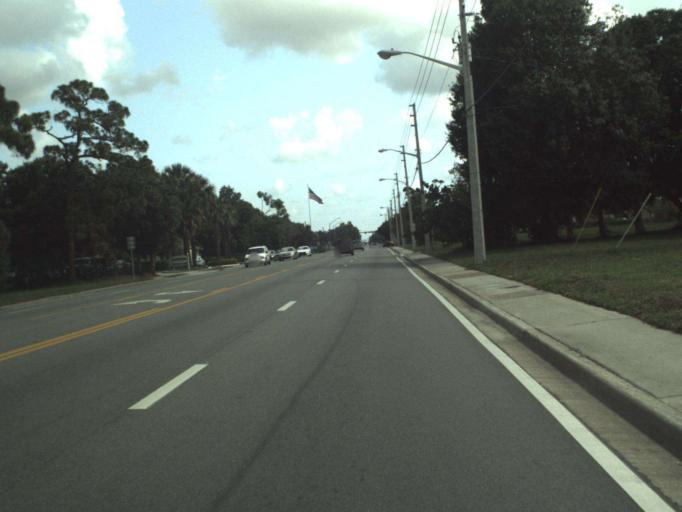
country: US
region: Florida
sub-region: Saint Lucie County
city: Fort Pierce South
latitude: 27.4335
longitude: -80.3501
